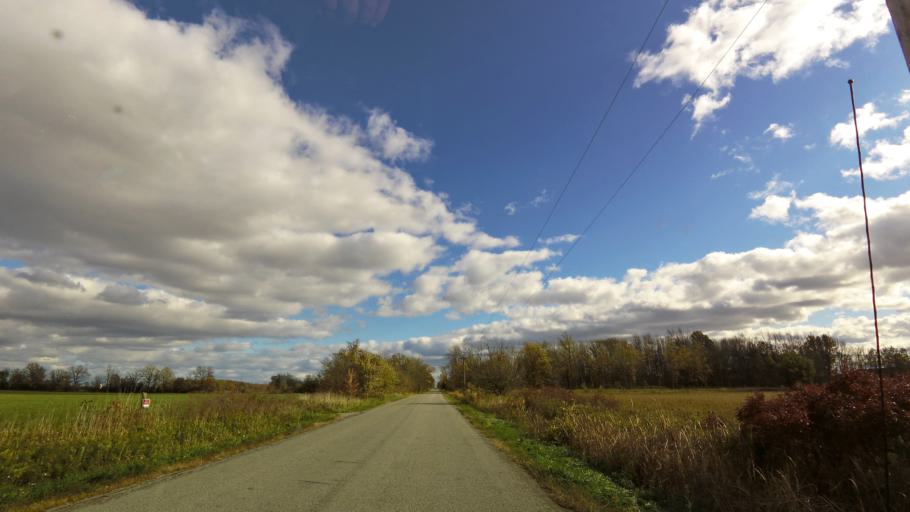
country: CA
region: Ontario
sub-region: Halton
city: Milton
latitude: 43.4548
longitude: -79.8636
